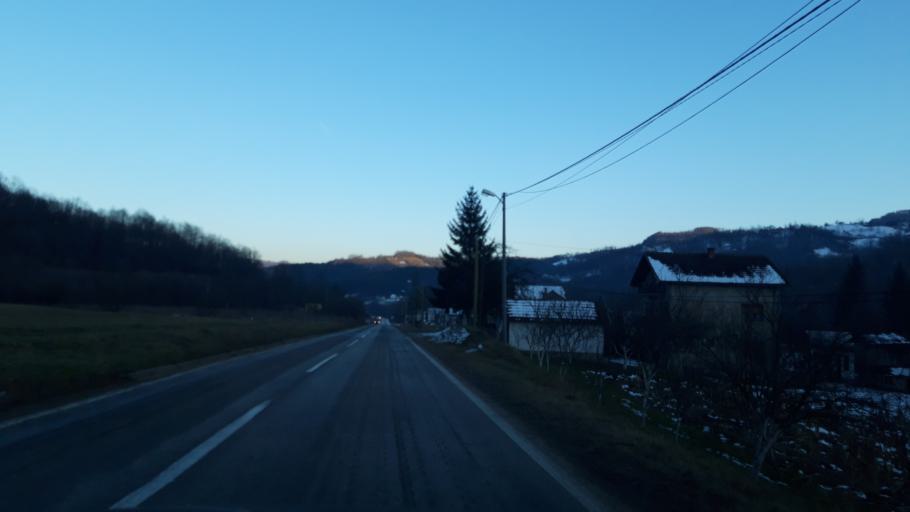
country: BA
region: Republika Srpska
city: Milici
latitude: 44.1643
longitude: 19.0573
